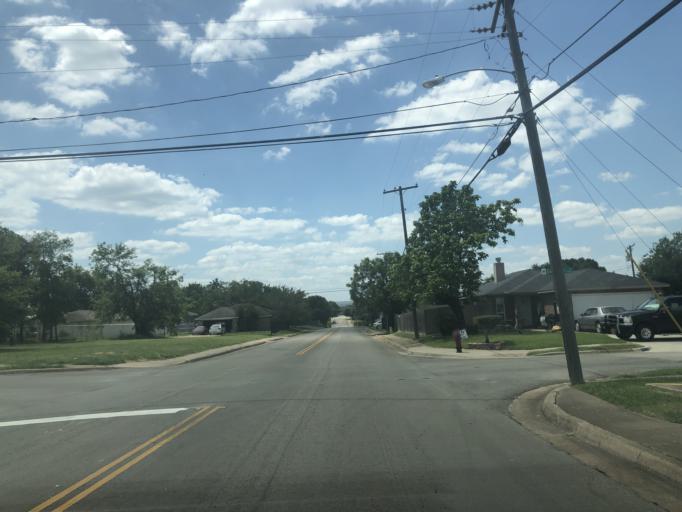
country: US
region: Texas
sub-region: Dallas County
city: Grand Prairie
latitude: 32.7392
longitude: -97.0291
